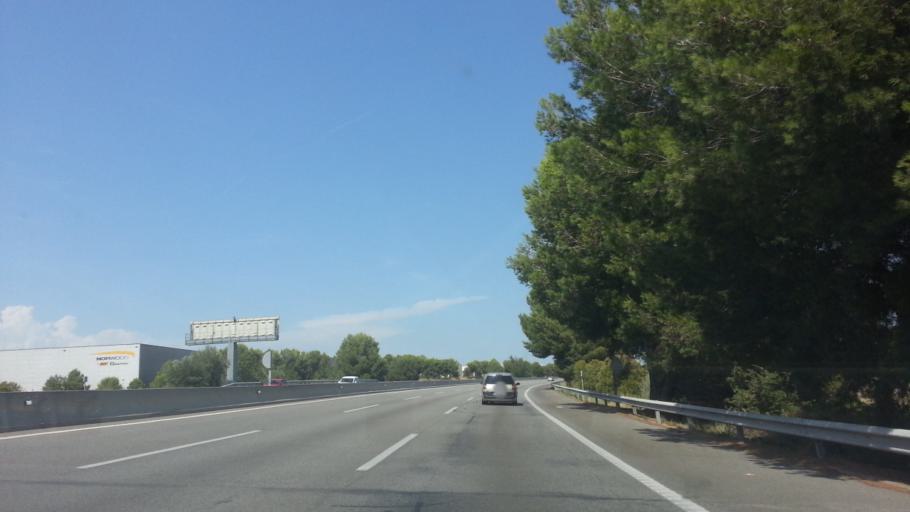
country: ES
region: Catalonia
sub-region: Provincia de Barcelona
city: La Granada
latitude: 41.3687
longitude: 1.7276
